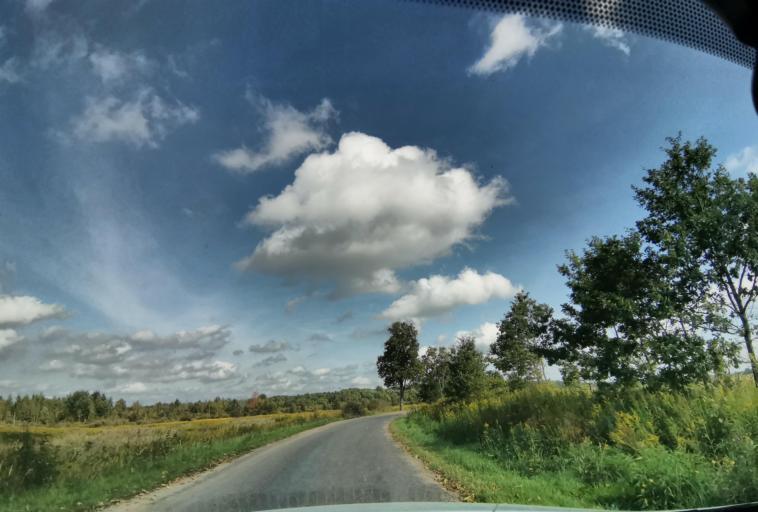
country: RU
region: Kaliningrad
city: Chernyakhovsk
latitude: 54.6630
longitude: 21.9559
